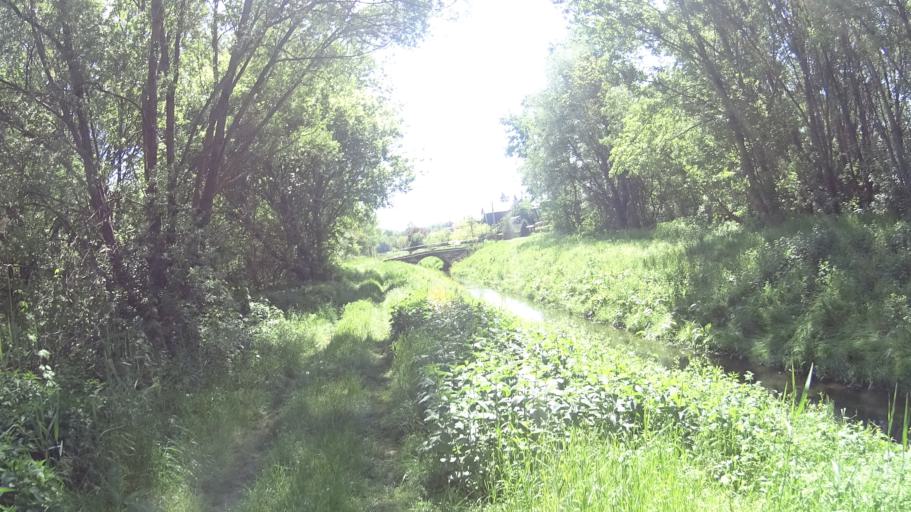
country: HU
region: Budapest
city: Budapest XXIII. keruelet
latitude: 47.3864
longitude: 19.1550
